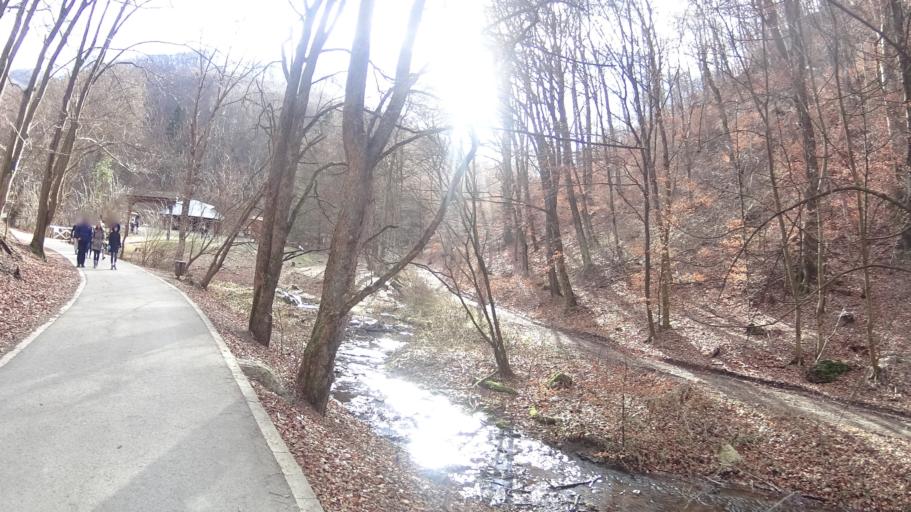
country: HU
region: Heves
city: Szilvasvarad
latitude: 48.0773
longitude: 20.4080
